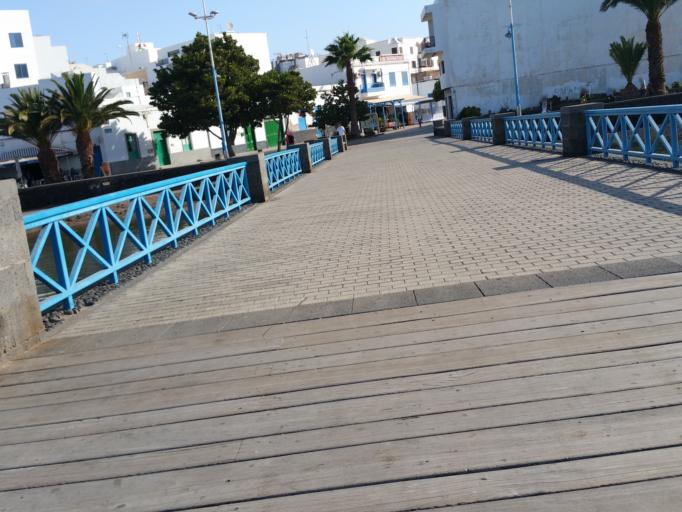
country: ES
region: Canary Islands
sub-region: Provincia de Las Palmas
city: Arrecife
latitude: 28.9610
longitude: -13.5444
